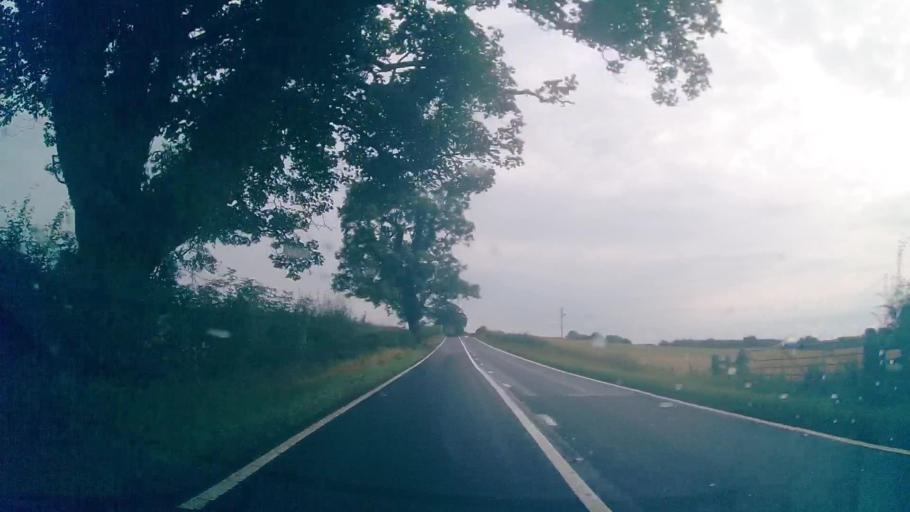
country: GB
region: Scotland
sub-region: Dumfries and Galloway
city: Locharbriggs
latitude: 55.0649
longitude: -3.5041
